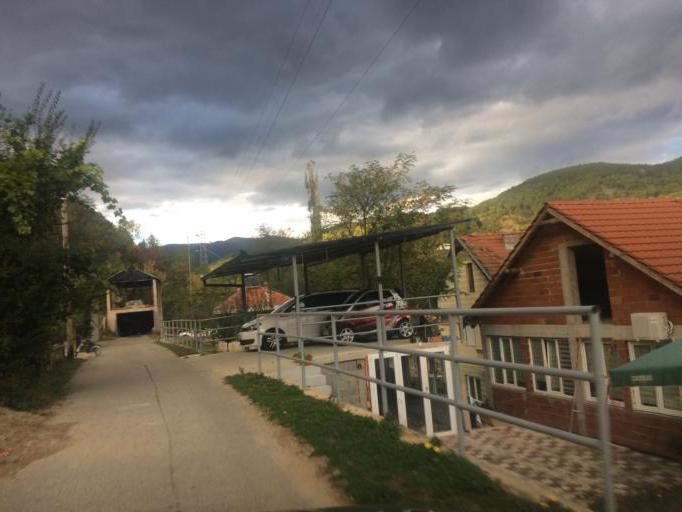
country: MK
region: Makedonska Kamenica
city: Makedonska Kamenica
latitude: 42.0262
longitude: 22.5843
